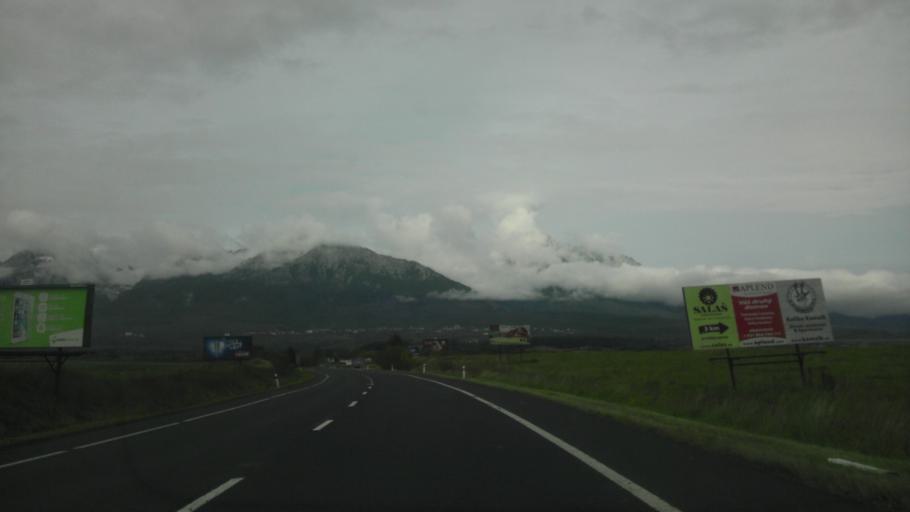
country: SK
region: Presovsky
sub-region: Okres Poprad
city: Poprad
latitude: 49.0823
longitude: 20.2681
